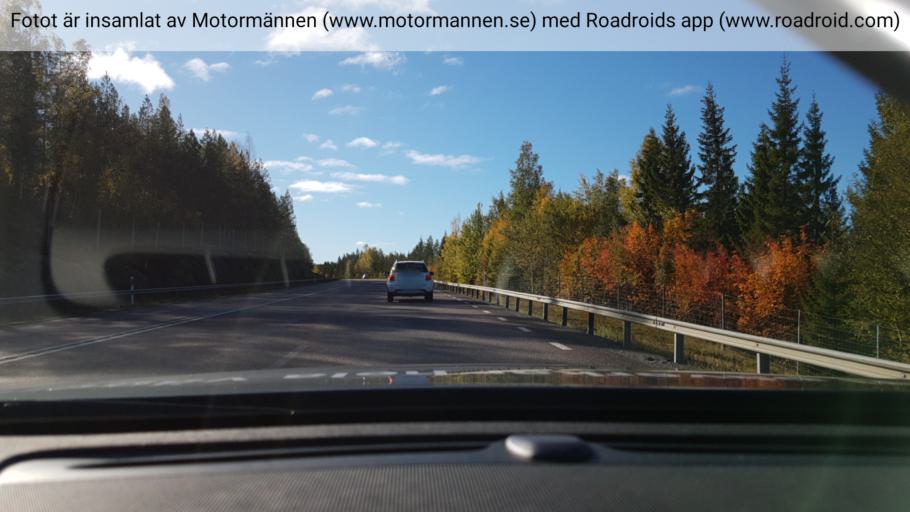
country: SE
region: Vaesterbotten
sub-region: Skelleftea Kommun
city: Burea
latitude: 64.4538
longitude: 21.2855
